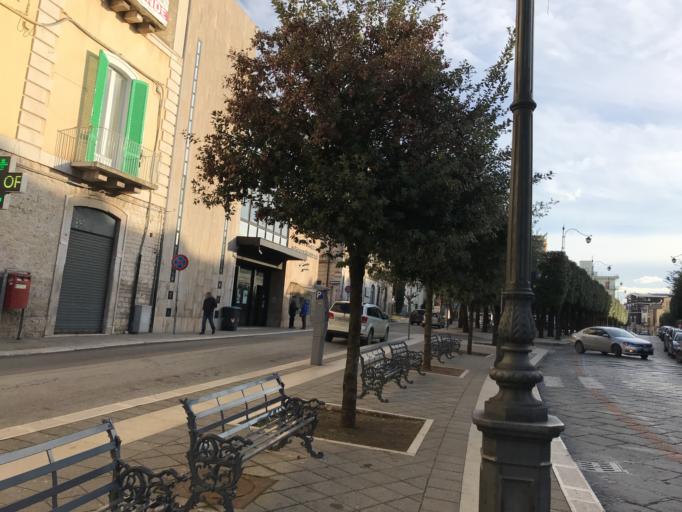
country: IT
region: Apulia
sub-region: Provincia di Bari
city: Corato
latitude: 41.1525
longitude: 16.4133
